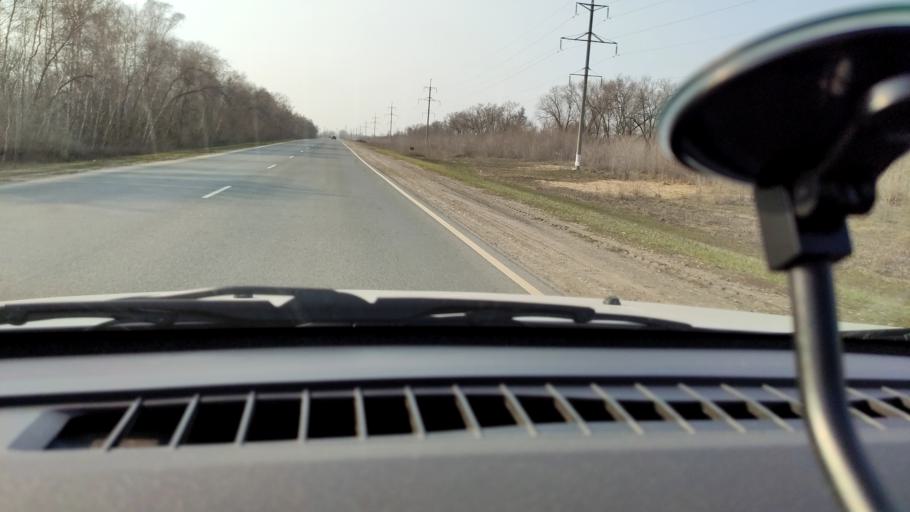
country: RU
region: Samara
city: Dubovyy Umet
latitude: 53.0991
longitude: 50.2627
